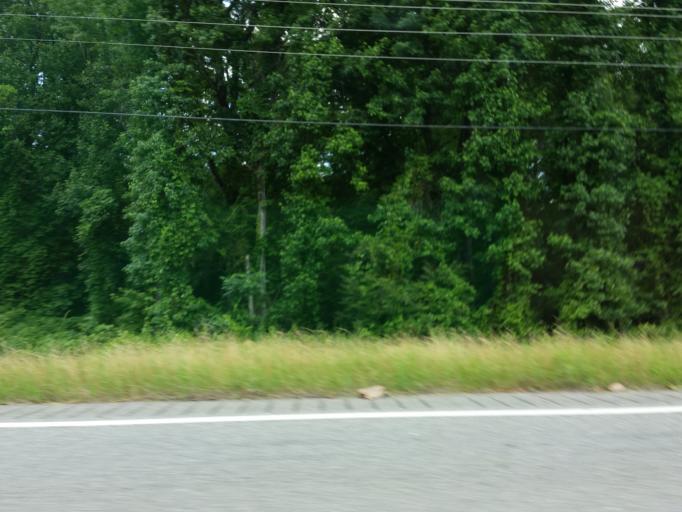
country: US
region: Alabama
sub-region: Sumter County
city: York
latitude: 32.4387
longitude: -88.2632
